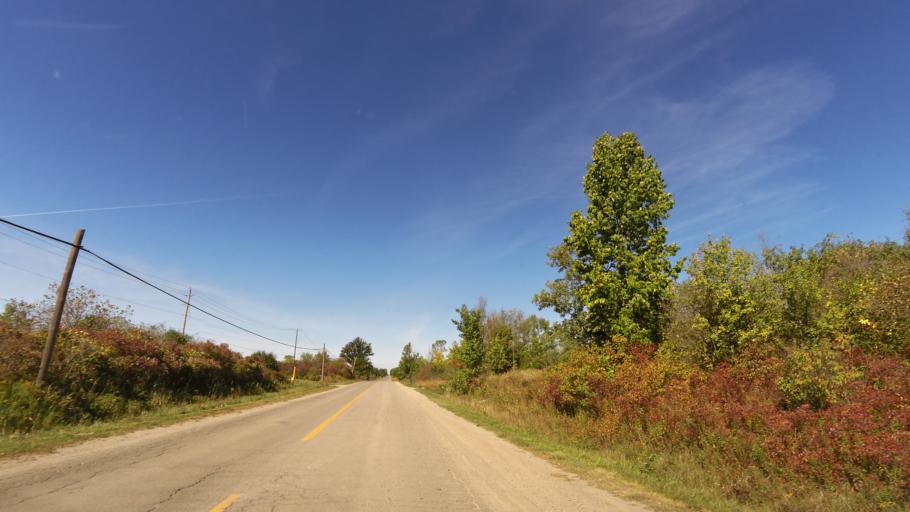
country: CA
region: Ontario
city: Ancaster
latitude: 43.0204
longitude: -80.0430
